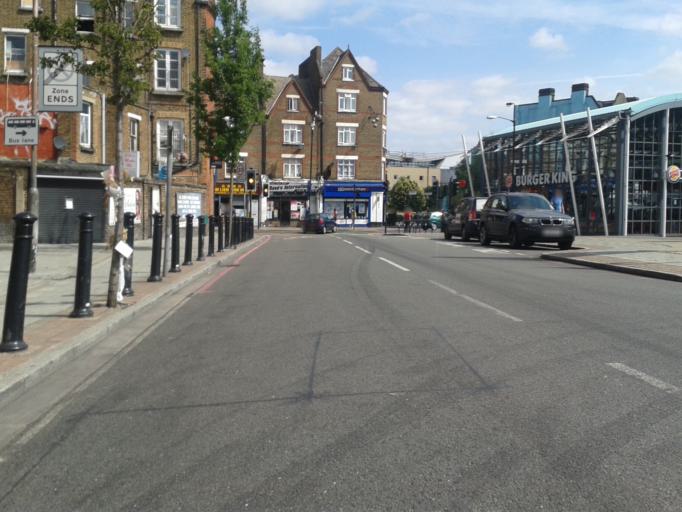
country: GB
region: England
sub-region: Greater London
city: Camberwell
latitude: 51.4729
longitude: -0.0714
